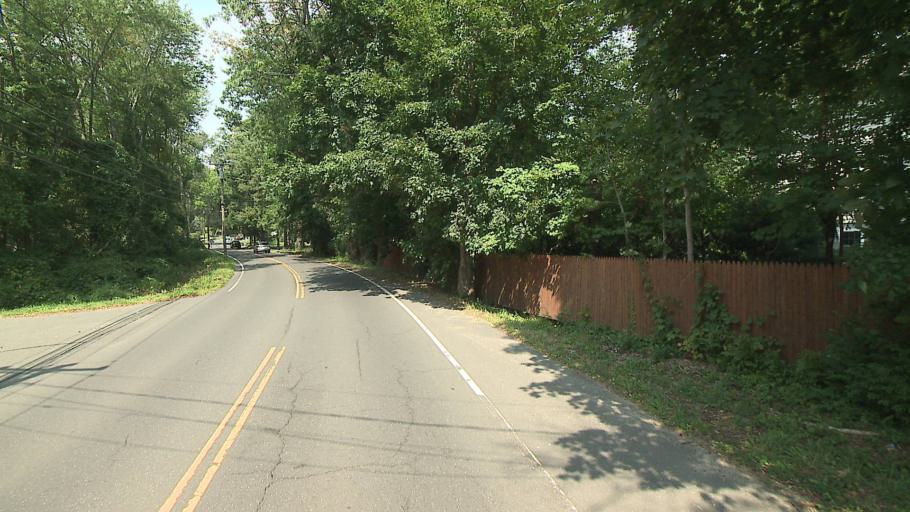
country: US
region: Connecticut
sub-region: Fairfield County
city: Ridgefield
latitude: 41.3112
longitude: -73.5103
